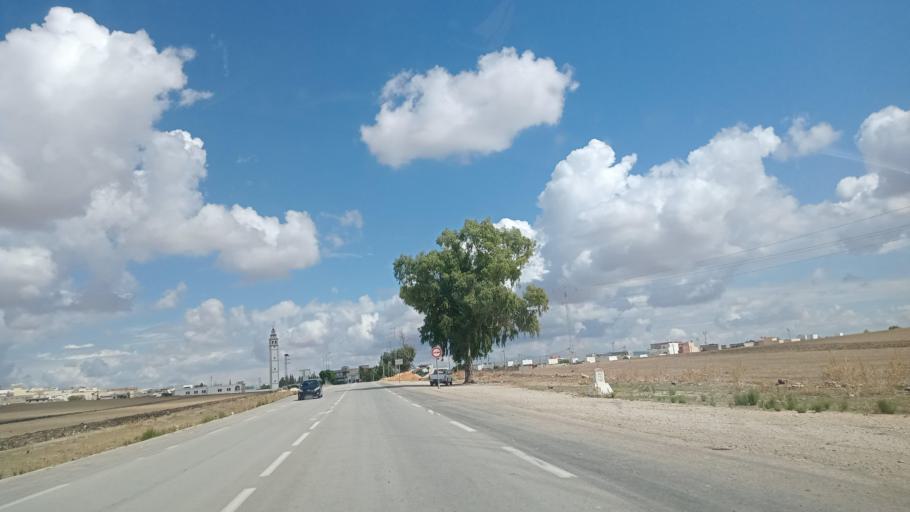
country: TN
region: Silyanah
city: Al Karib
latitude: 36.3223
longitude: 9.1275
